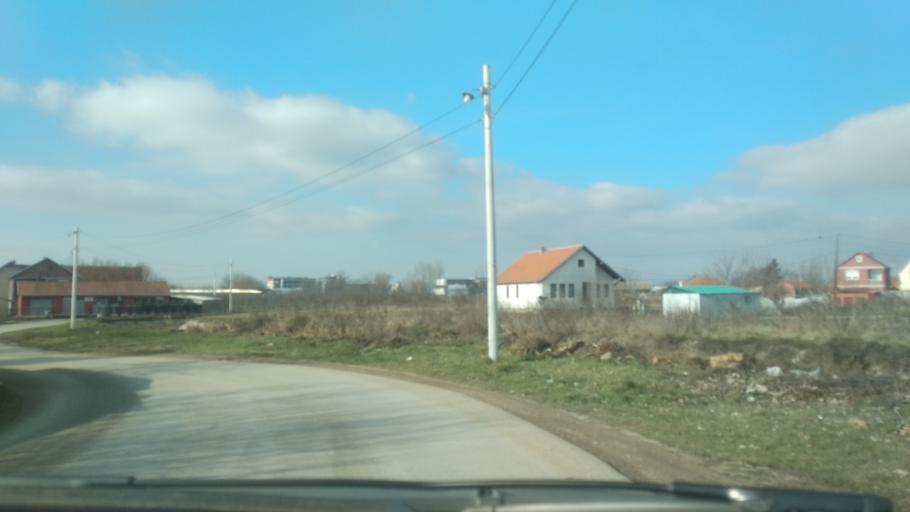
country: XK
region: Pristina
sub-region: Lipjan
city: Lipljan
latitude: 42.5944
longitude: 21.1389
